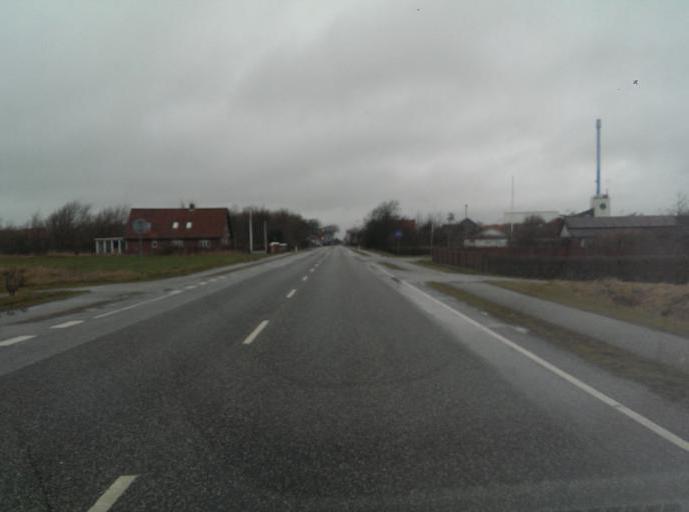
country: DK
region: Central Jutland
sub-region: Ringkobing-Skjern Kommune
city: Ringkobing
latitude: 56.1420
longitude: 8.2822
